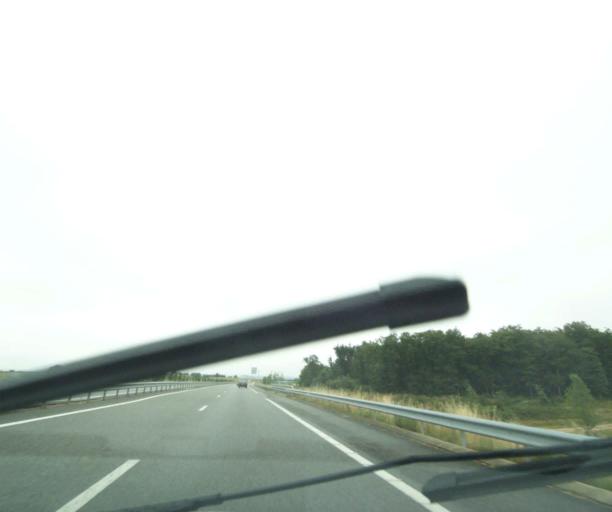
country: FR
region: Midi-Pyrenees
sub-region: Departement du Tarn
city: Le Garric
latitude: 44.0264
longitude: 2.1881
